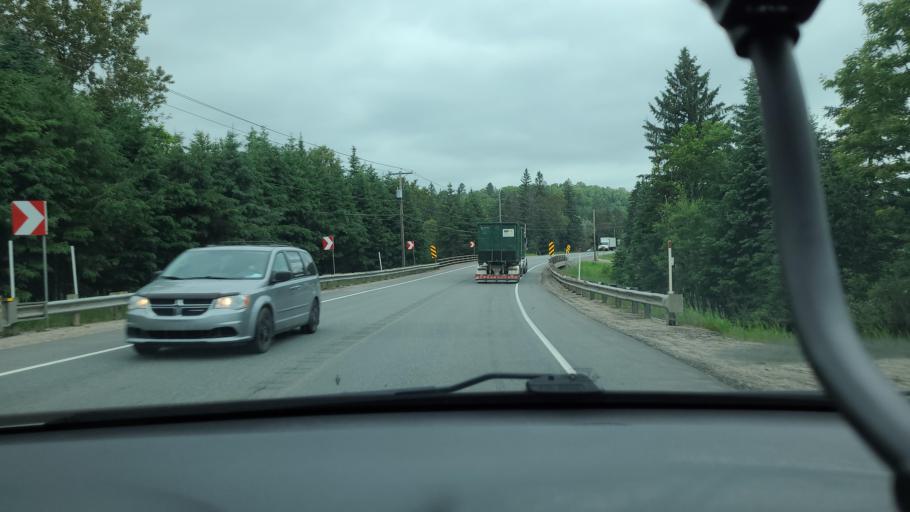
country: CA
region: Quebec
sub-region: Laurentides
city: Labelle
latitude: 46.3101
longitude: -74.7900
